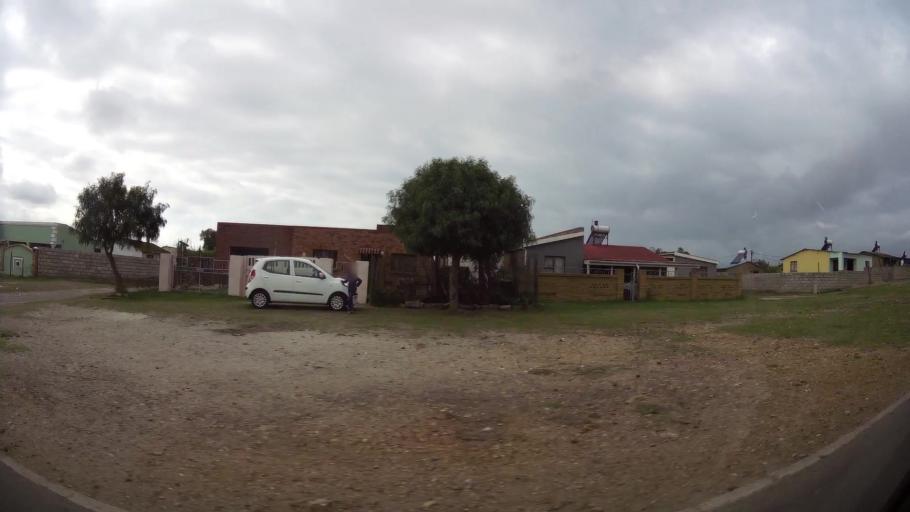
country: ZA
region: Eastern Cape
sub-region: Nelson Mandela Bay Metropolitan Municipality
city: Port Elizabeth
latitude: -33.8833
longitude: 25.6035
